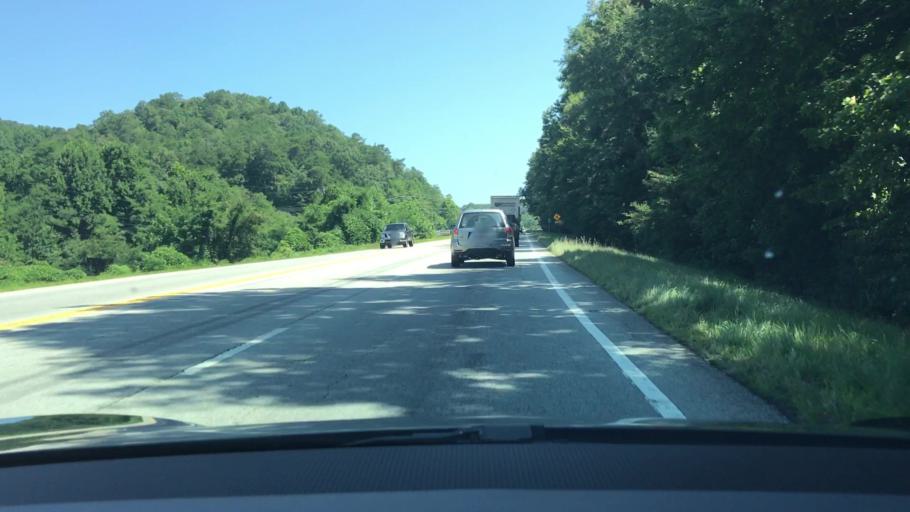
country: US
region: Georgia
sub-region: Rabun County
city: Clayton
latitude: 34.8961
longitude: -83.3930
